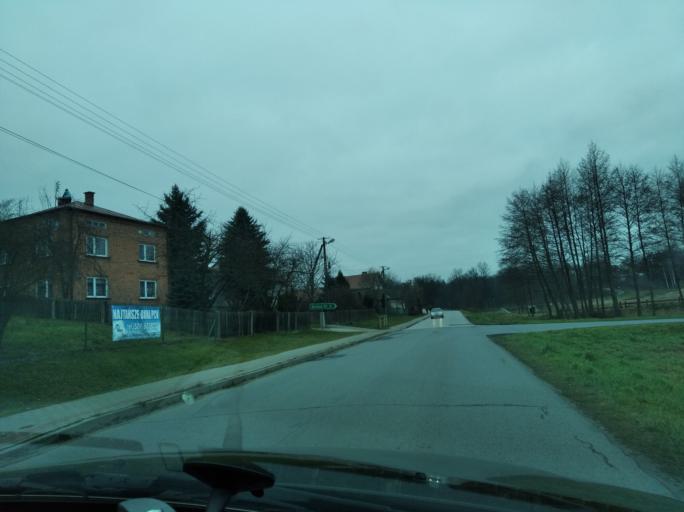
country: PL
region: Subcarpathian Voivodeship
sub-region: Powiat lancucki
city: Rakszawa
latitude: 50.1758
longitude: 22.2352
